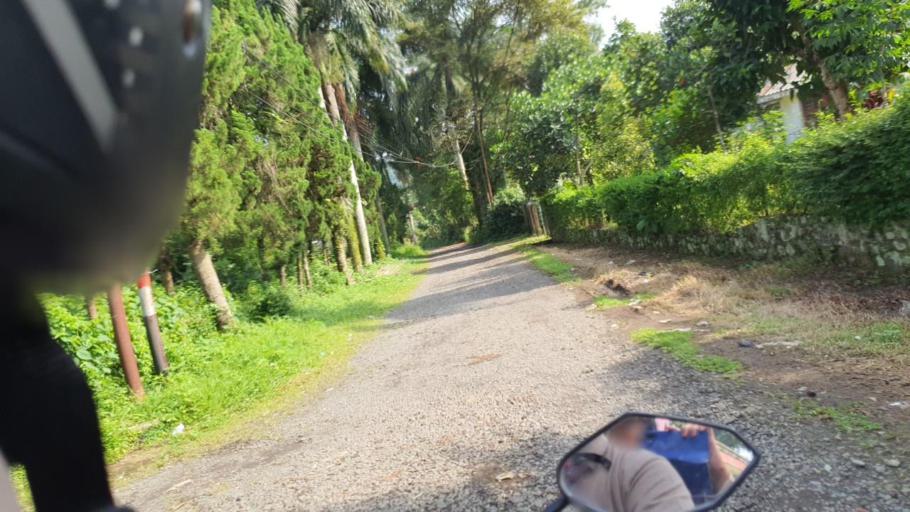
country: ID
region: West Java
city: Caringin
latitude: -6.6551
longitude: 106.8712
